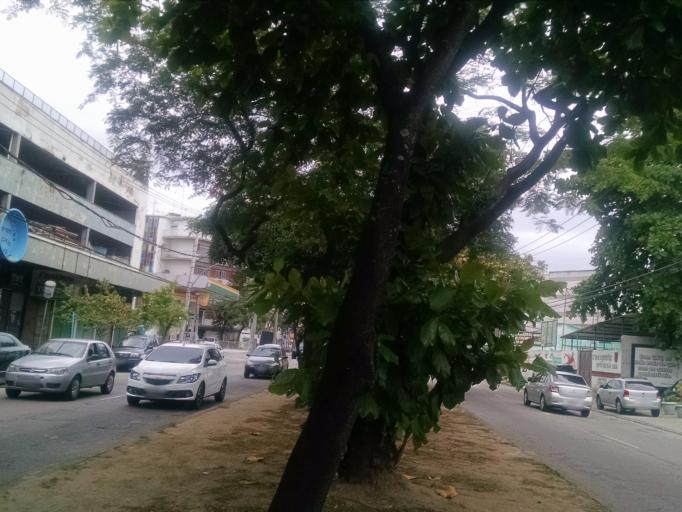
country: BR
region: Rio de Janeiro
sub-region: Duque De Caxias
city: Duque de Caxias
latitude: -22.8340
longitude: -43.3090
